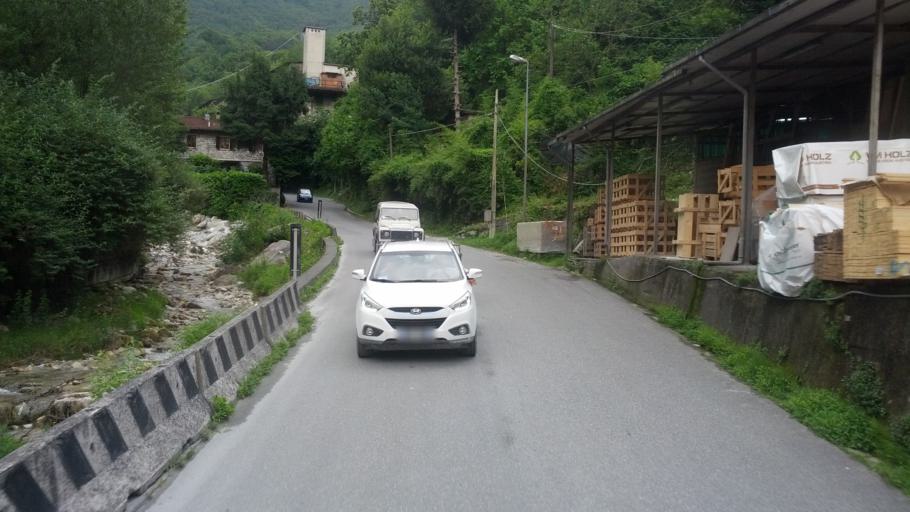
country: IT
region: Tuscany
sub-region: Provincia di Massa-Carrara
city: Massa
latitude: 44.0810
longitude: 10.1247
